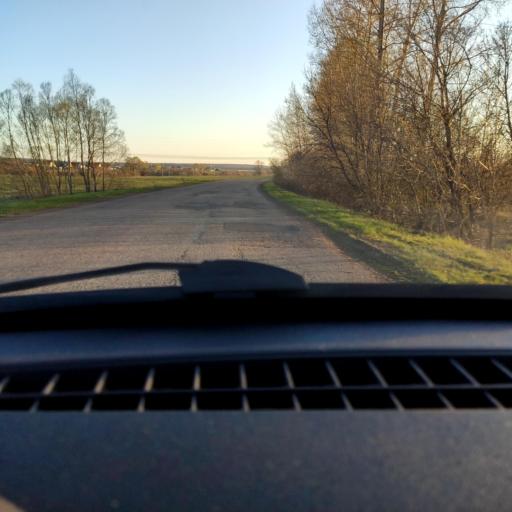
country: RU
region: Bashkortostan
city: Avdon
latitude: 54.4917
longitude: 55.6061
